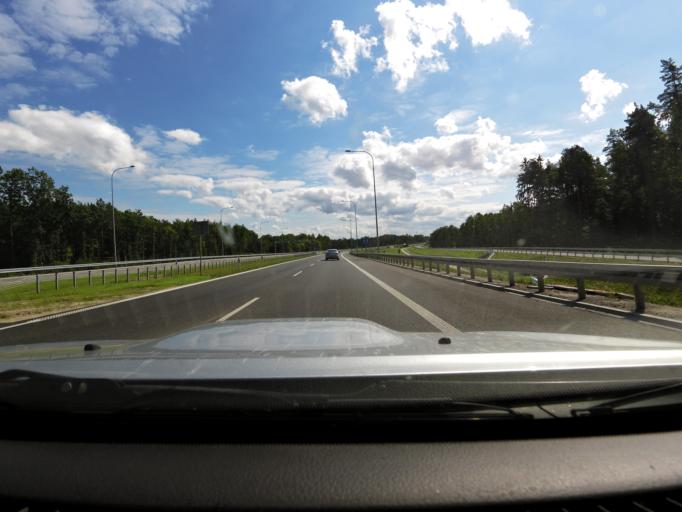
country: PL
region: Warmian-Masurian Voivodeship
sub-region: Powiat ostrodzki
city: Ostroda
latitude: 53.7279
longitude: 19.9393
